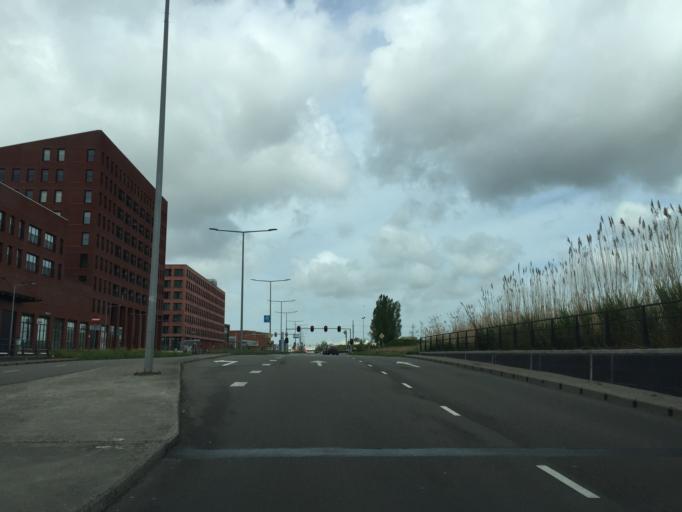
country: NL
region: South Holland
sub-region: Gemeente Den Haag
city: Ypenburg
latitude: 52.0653
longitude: 4.4038
